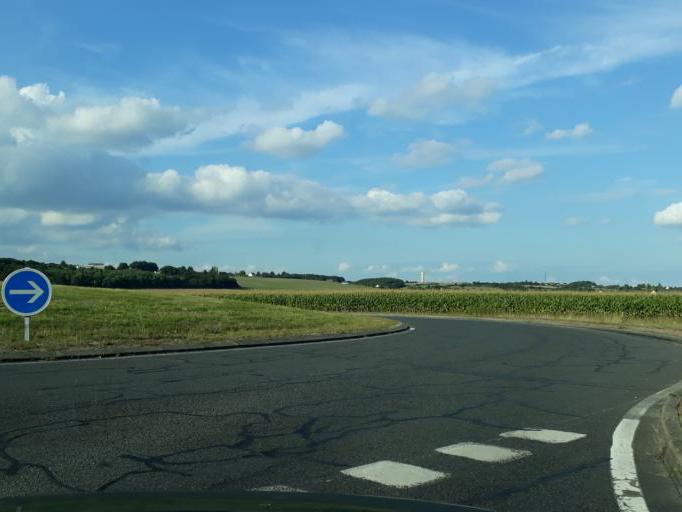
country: FR
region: Centre
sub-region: Departement du Loir-et-Cher
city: Moree
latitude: 47.8909
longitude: 1.1836
